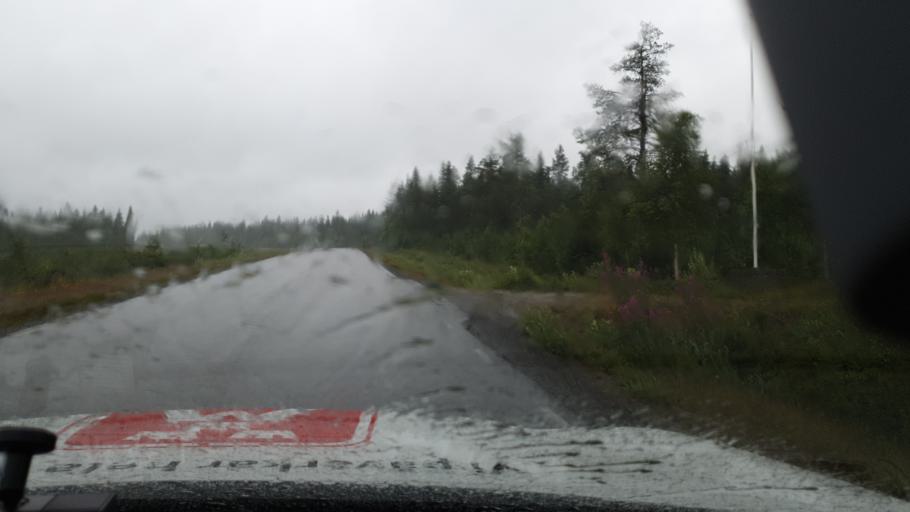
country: SE
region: Vaesterbotten
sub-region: Skelleftea Kommun
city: Storvik
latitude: 65.3260
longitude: 20.7546
